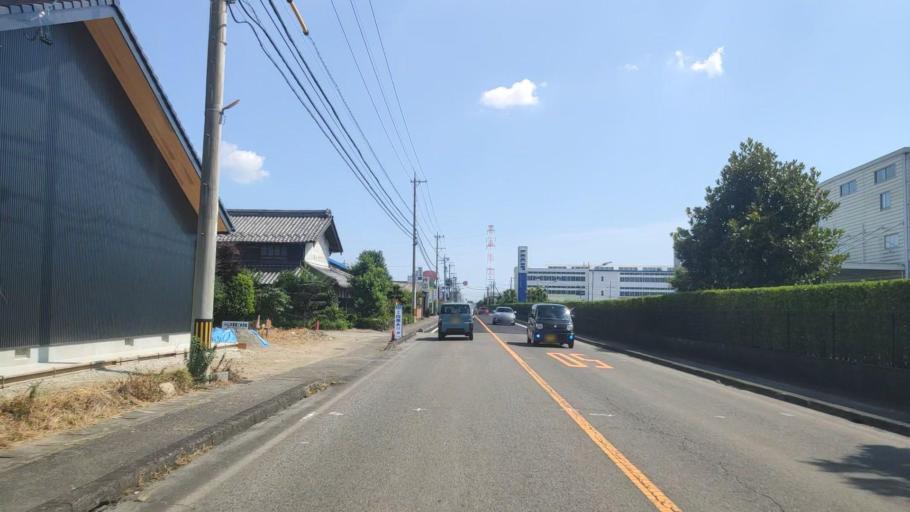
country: JP
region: Gifu
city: Godo
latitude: 35.4669
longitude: 136.6754
